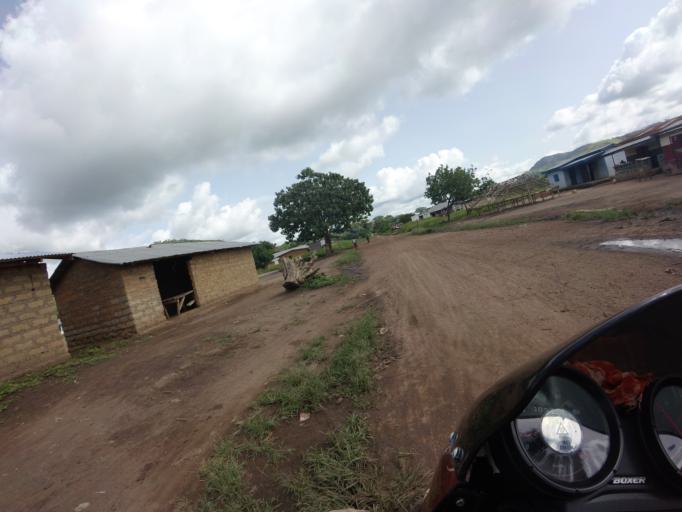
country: SL
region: Eastern Province
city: Tombu
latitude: 8.6022
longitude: -10.6967
